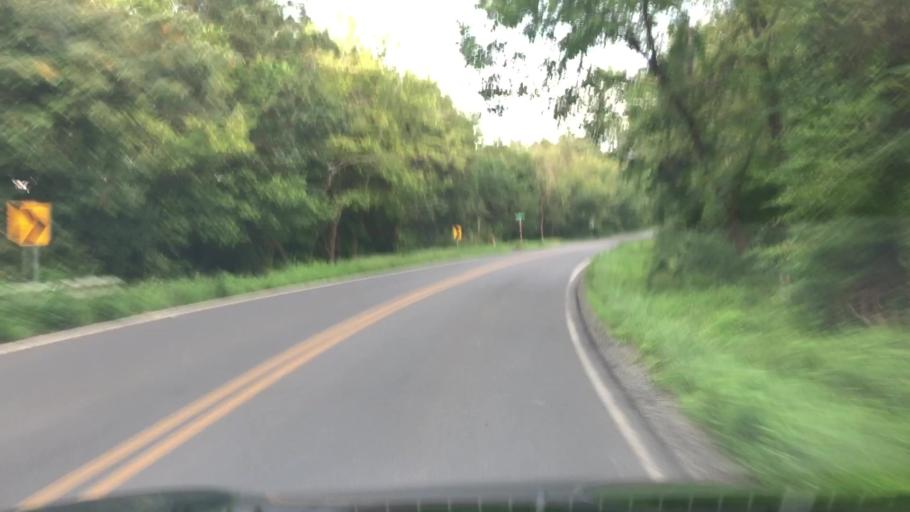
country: US
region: Virginia
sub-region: Fauquier County
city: Bealeton
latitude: 38.5967
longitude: -77.7075
